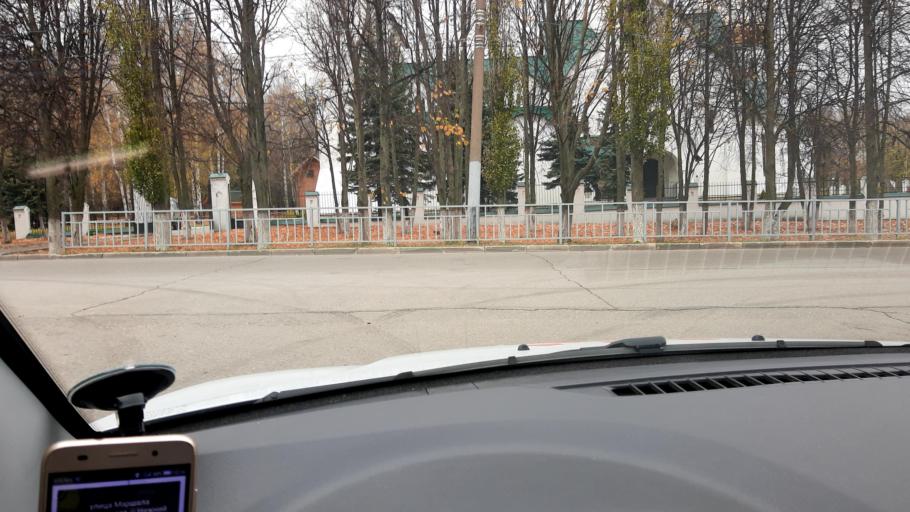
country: RU
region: Nizjnij Novgorod
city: Nizhniy Novgorod
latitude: 56.2292
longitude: 43.9428
